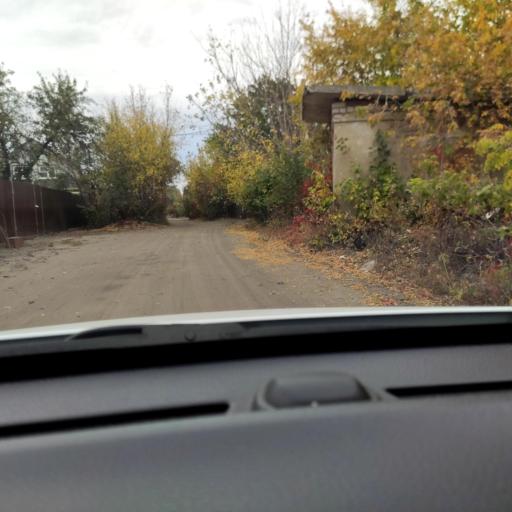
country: RU
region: Voronezj
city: Maslovka
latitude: 51.6055
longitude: 39.2786
